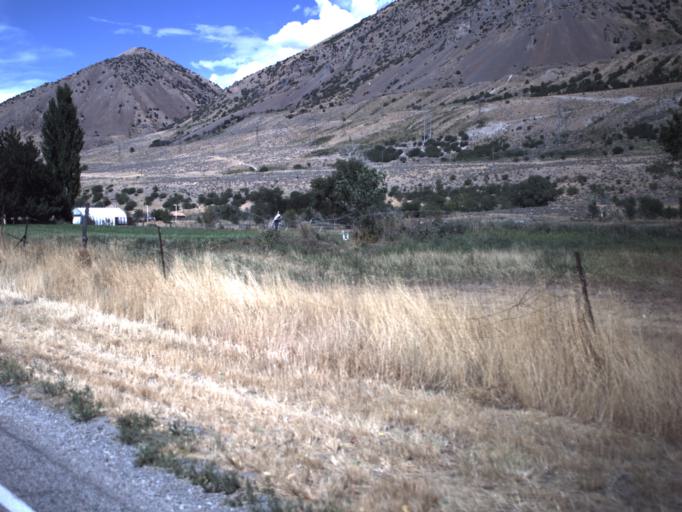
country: US
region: Utah
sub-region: Box Elder County
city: Elwood
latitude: 41.7030
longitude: -112.0901
